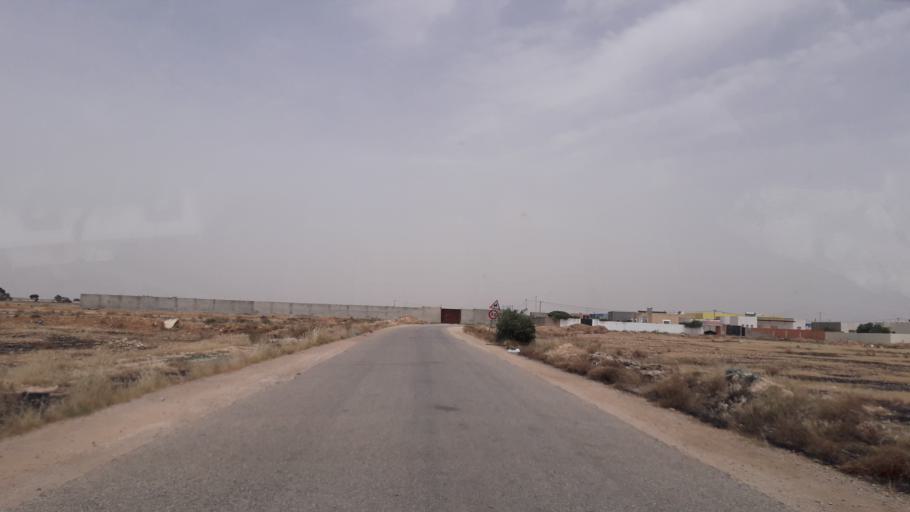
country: TN
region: Safaqis
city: Al Qarmadah
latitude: 34.8460
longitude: 10.7556
